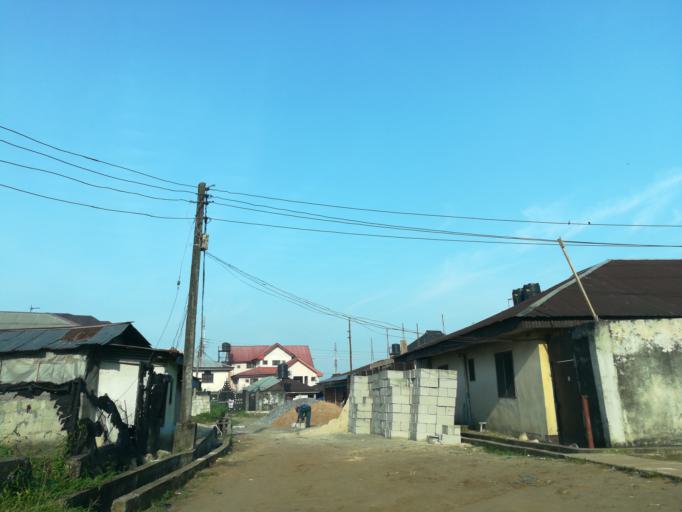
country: NG
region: Rivers
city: Port Harcourt
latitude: 4.8195
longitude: 7.0200
